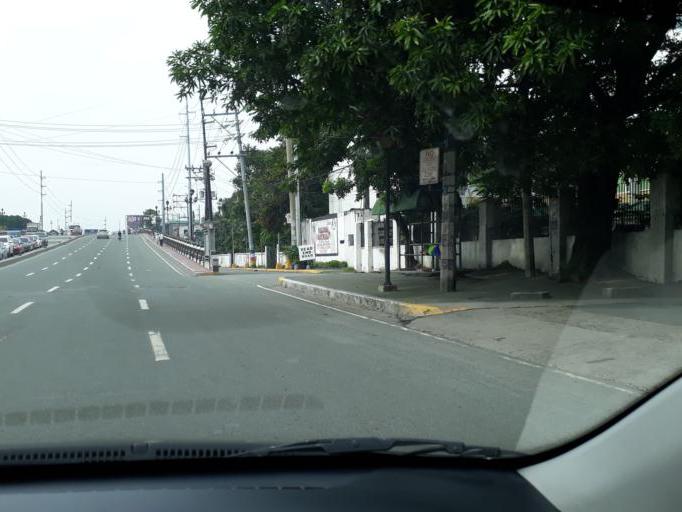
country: PH
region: Metro Manila
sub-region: City of Manila
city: Quiapo
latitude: 14.5930
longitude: 121.0017
